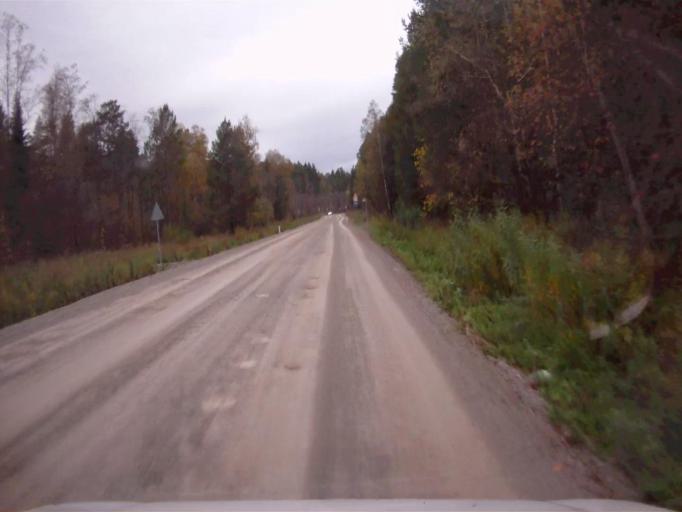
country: RU
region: Chelyabinsk
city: Nyazepetrovsk
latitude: 56.0439
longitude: 59.5058
